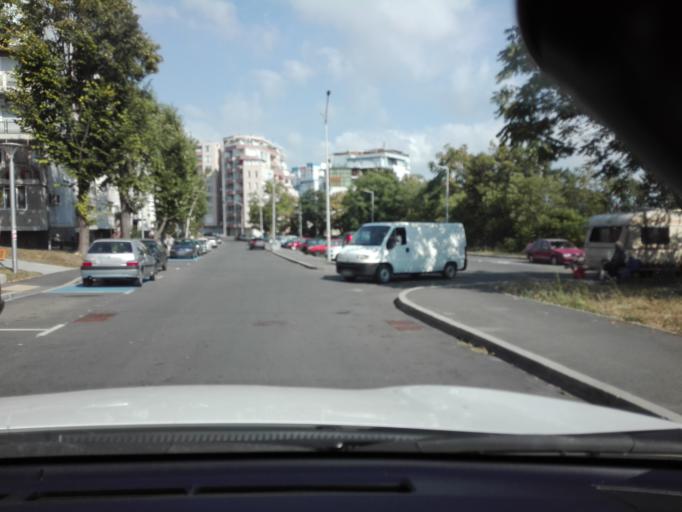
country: BG
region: Burgas
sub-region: Obshtina Burgas
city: Burgas
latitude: 42.4580
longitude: 27.4235
